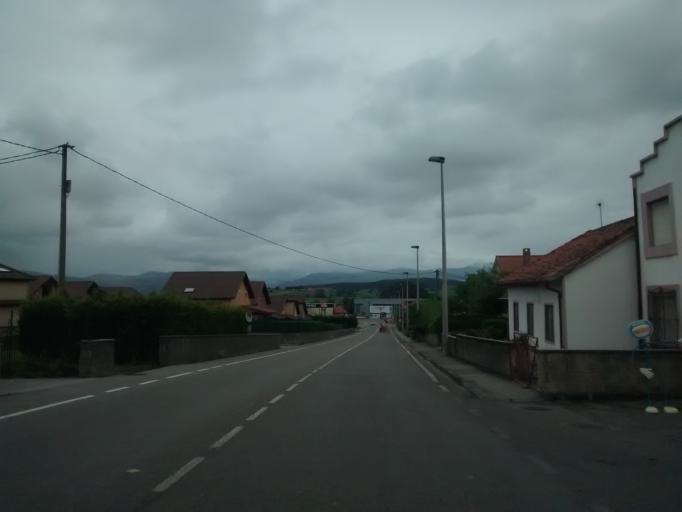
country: ES
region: Cantabria
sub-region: Provincia de Cantabria
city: Suances
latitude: 43.3996
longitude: -4.0484
